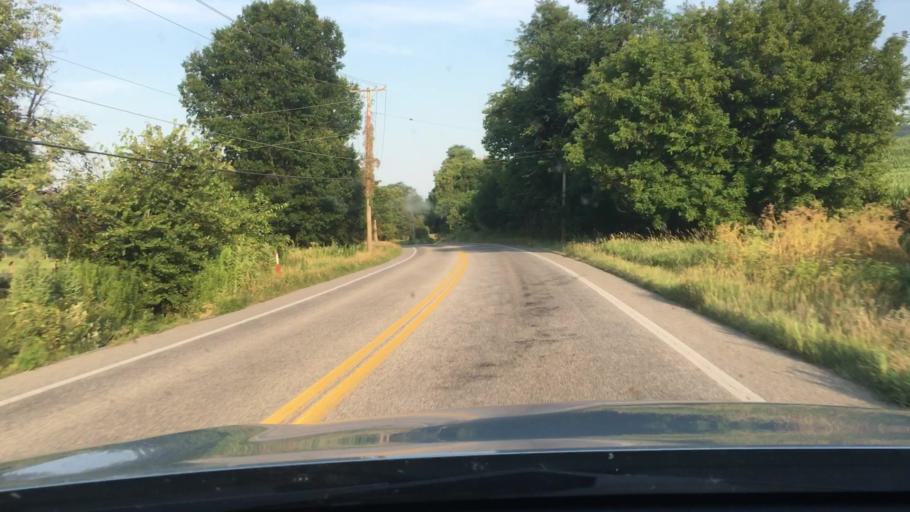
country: US
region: Pennsylvania
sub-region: Cumberland County
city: Boiling Springs
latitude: 40.1507
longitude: -77.0750
